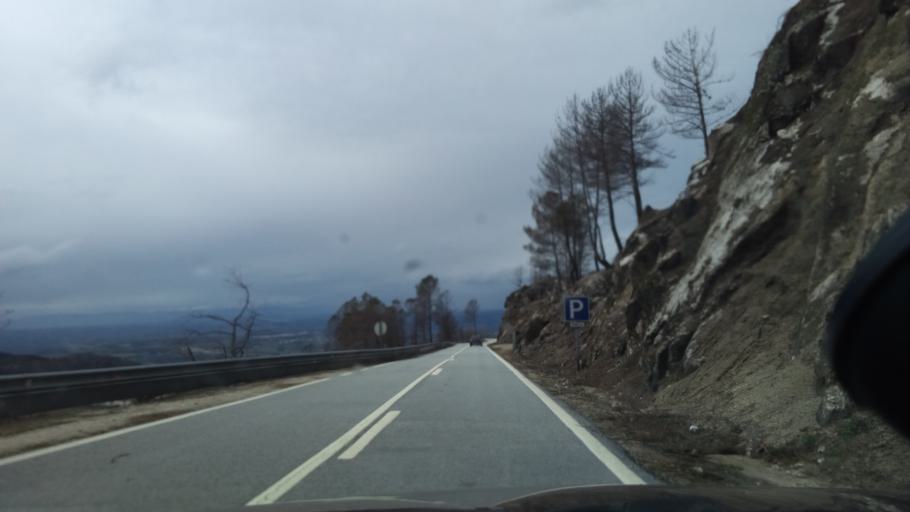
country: PT
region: Guarda
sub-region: Manteigas
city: Manteigas
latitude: 40.4636
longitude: -7.5884
